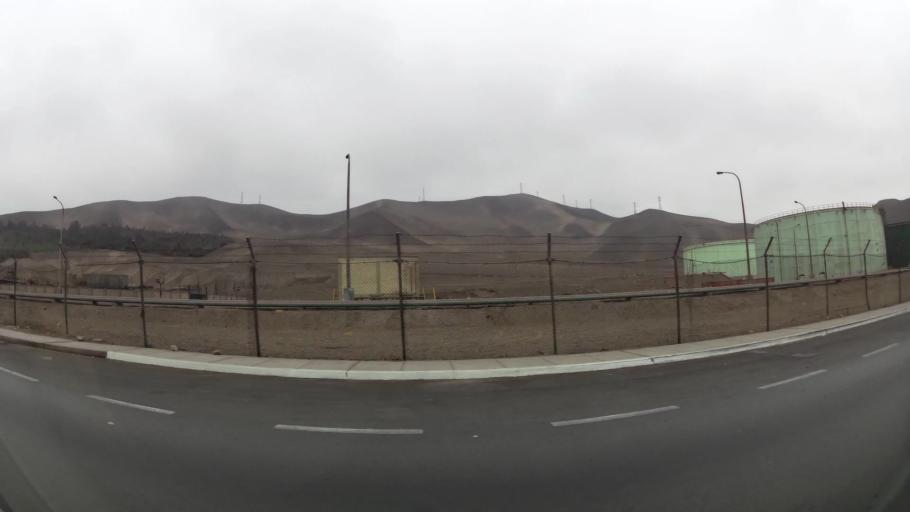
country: PE
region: Lima
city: Ventanilla
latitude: -11.9235
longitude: -77.1292
